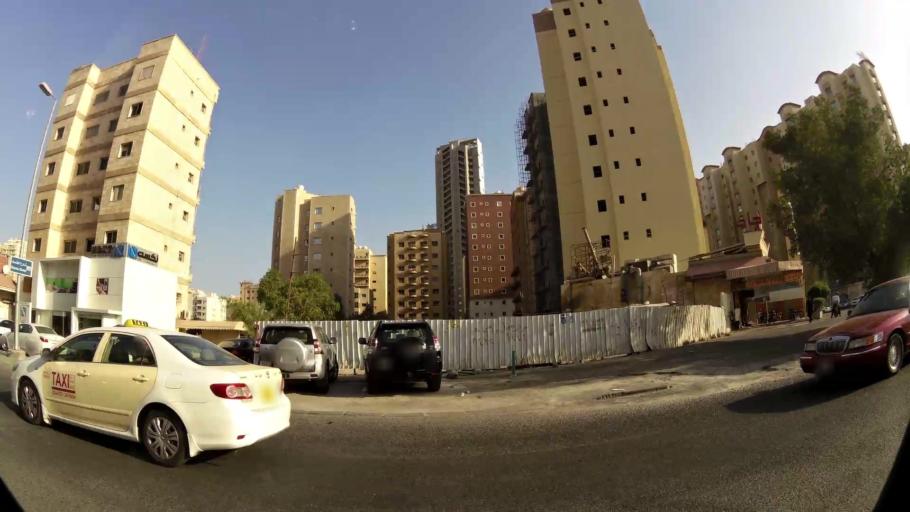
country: KW
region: Muhafazat Hawalli
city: As Salimiyah
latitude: 29.3373
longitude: 48.0877
